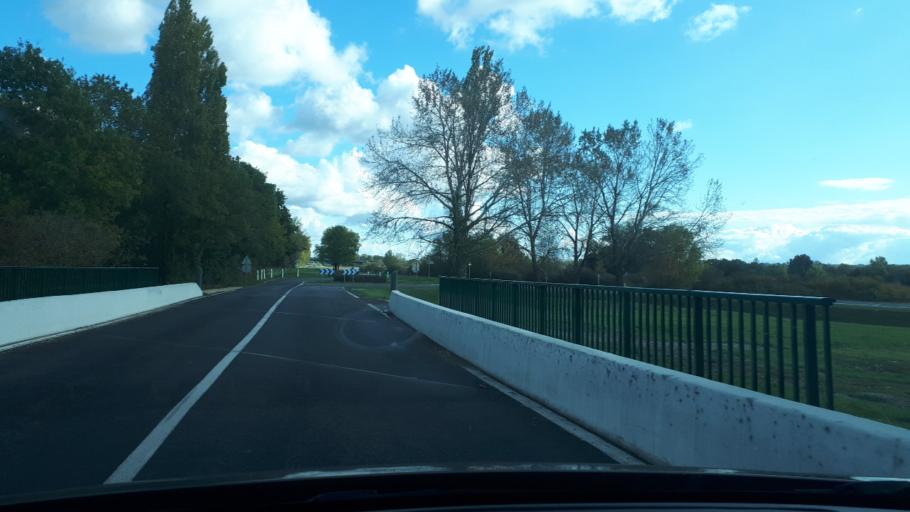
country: FR
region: Centre
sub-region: Departement du Loir-et-Cher
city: Mareuil-sur-Cher
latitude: 47.3097
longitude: 1.3382
